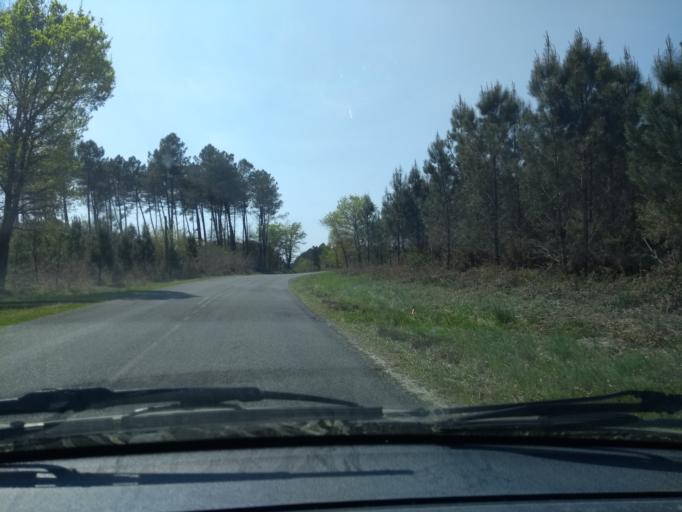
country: FR
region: Aquitaine
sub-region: Departement de la Gironde
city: Belin-Beliet
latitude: 44.5228
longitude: -0.7411
